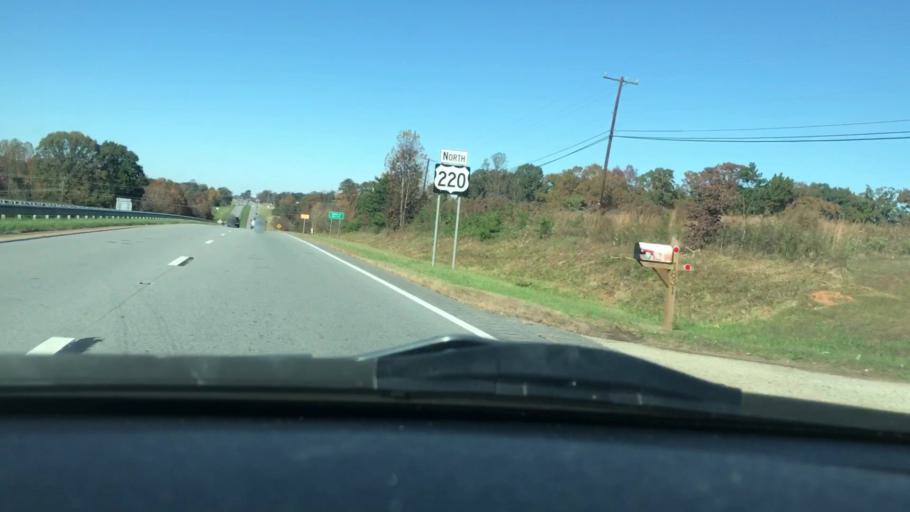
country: US
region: North Carolina
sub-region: Guilford County
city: Stokesdale
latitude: 36.2982
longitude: -79.9404
